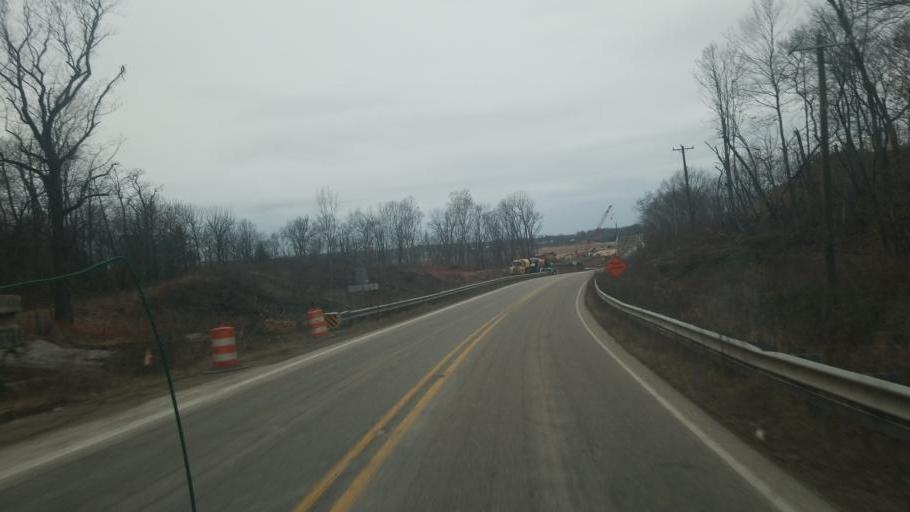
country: US
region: Indiana
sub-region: Clay County
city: Middlebury
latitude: 39.3831
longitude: -87.0167
